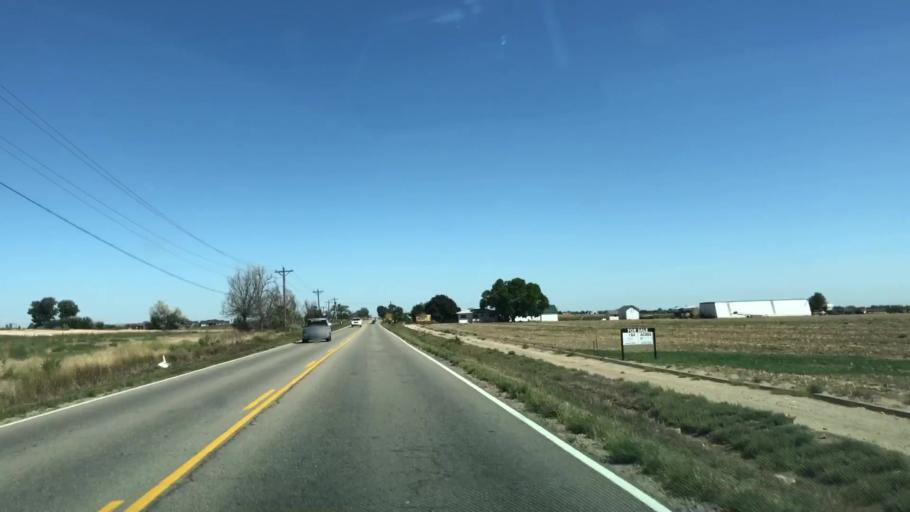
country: US
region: Colorado
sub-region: Weld County
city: Windsor
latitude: 40.5228
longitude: -104.9337
